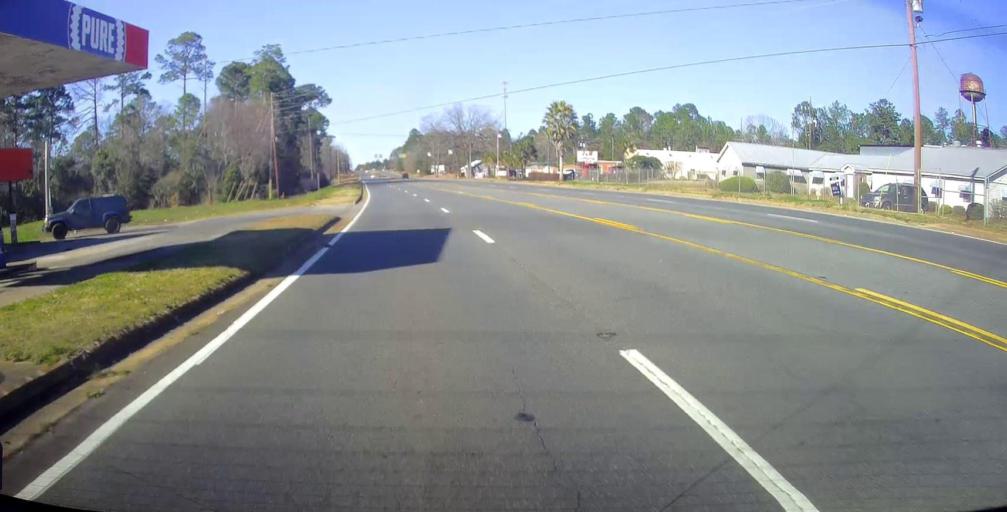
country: US
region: Georgia
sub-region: Sumter County
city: Americus
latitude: 32.0907
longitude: -84.2406
